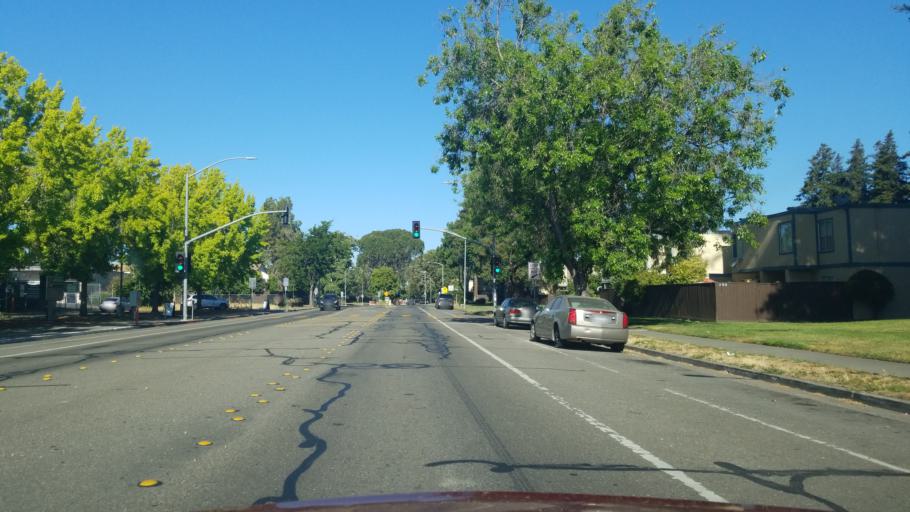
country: US
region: California
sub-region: Sonoma County
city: Roseland
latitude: 38.4417
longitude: -122.7363
